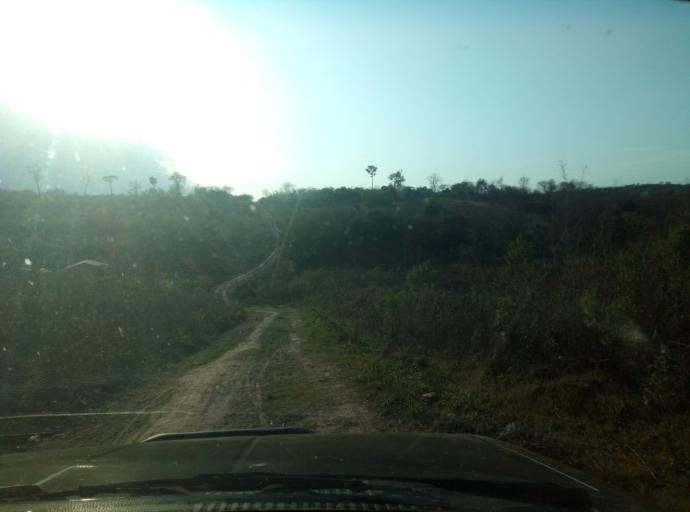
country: PY
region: Caaguazu
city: Doctor Cecilio Baez
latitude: -25.1989
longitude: -56.1206
